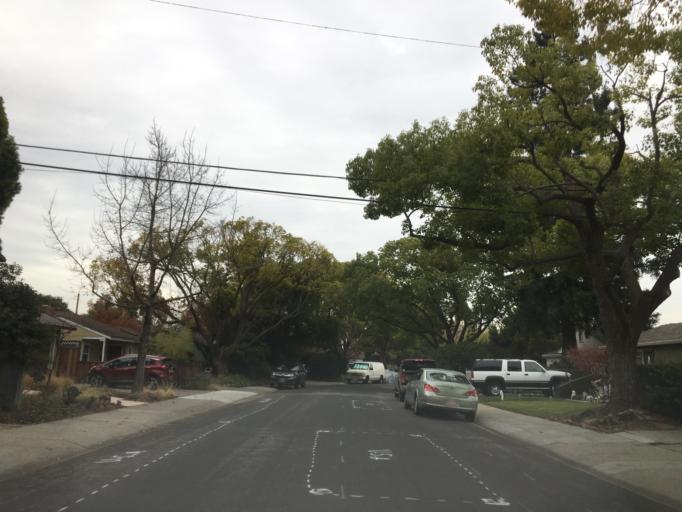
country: US
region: California
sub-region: Santa Clara County
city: Palo Alto
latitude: 37.4360
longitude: -122.1305
